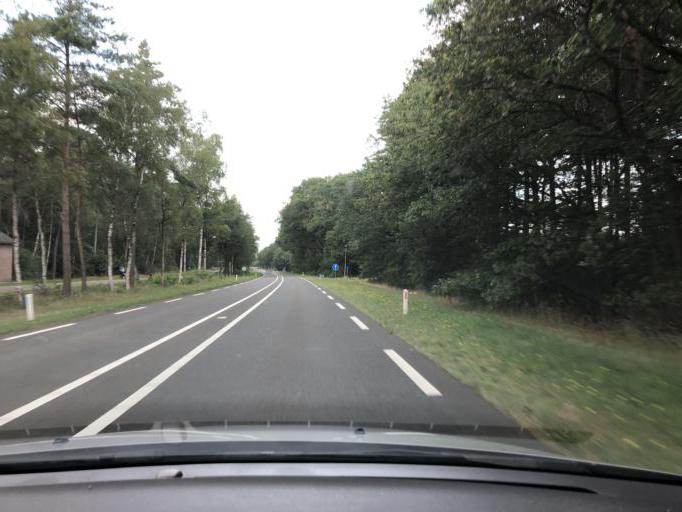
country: NL
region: Overijssel
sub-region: Gemeente Twenterand
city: Den Ham
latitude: 52.4782
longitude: 6.4277
